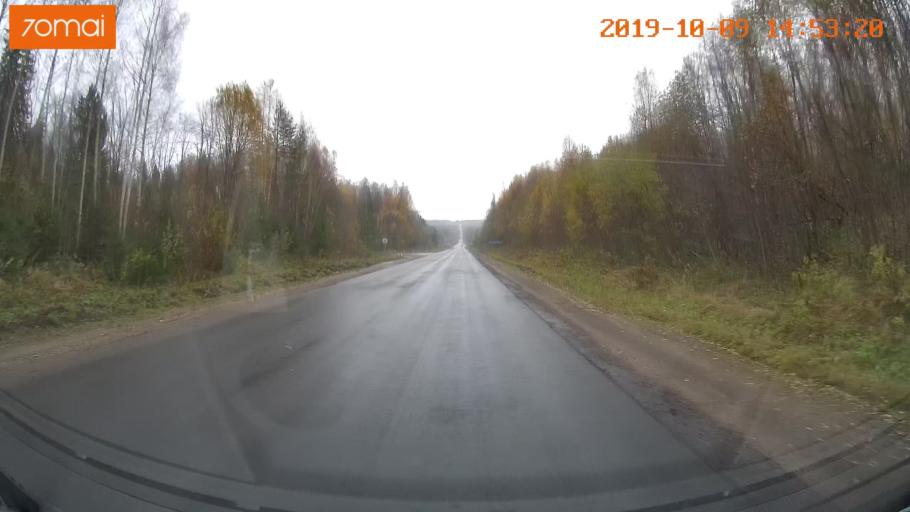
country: RU
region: Kostroma
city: Chistyye Bory
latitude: 58.3689
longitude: 41.6378
